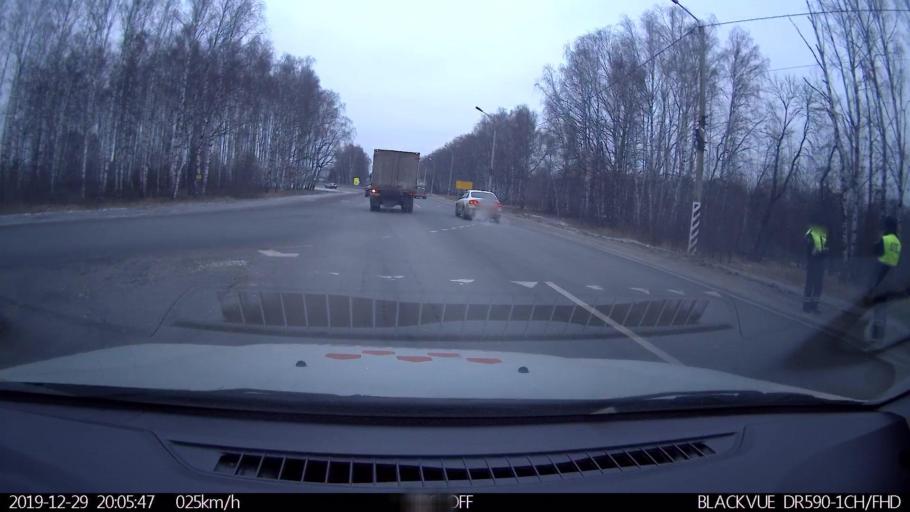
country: RU
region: Nizjnij Novgorod
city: Neklyudovo
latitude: 56.3934
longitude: 44.0099
